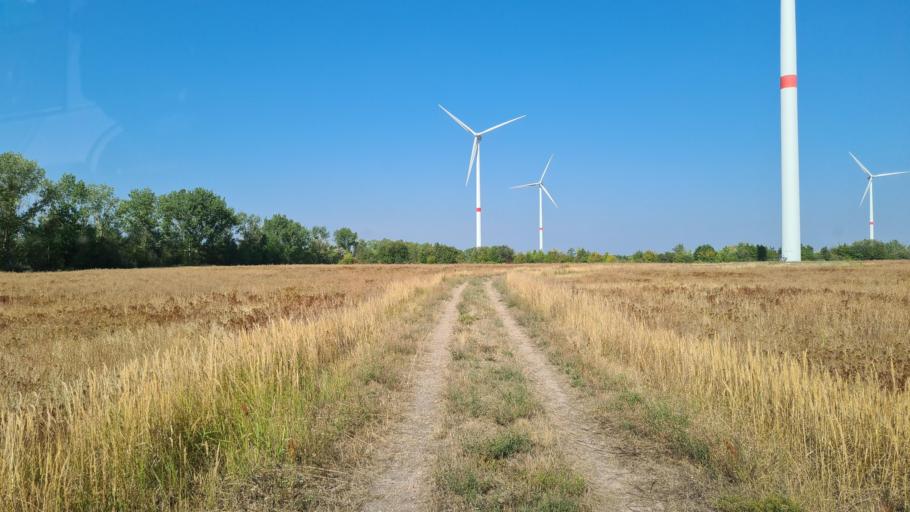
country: DE
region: Brandenburg
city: Sallgast
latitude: 51.5528
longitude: 13.8337
